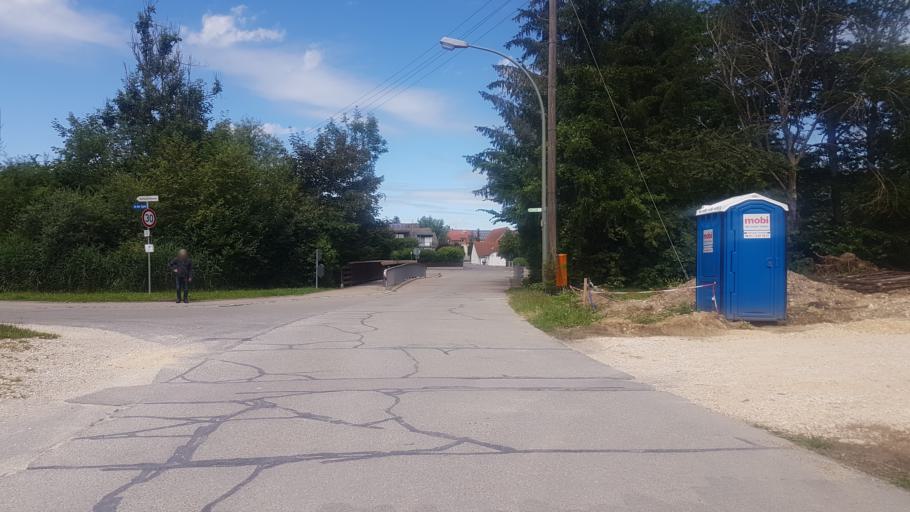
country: DE
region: Bavaria
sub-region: Swabia
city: Hochstadt an der Donau
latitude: 48.5932
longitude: 10.5418
